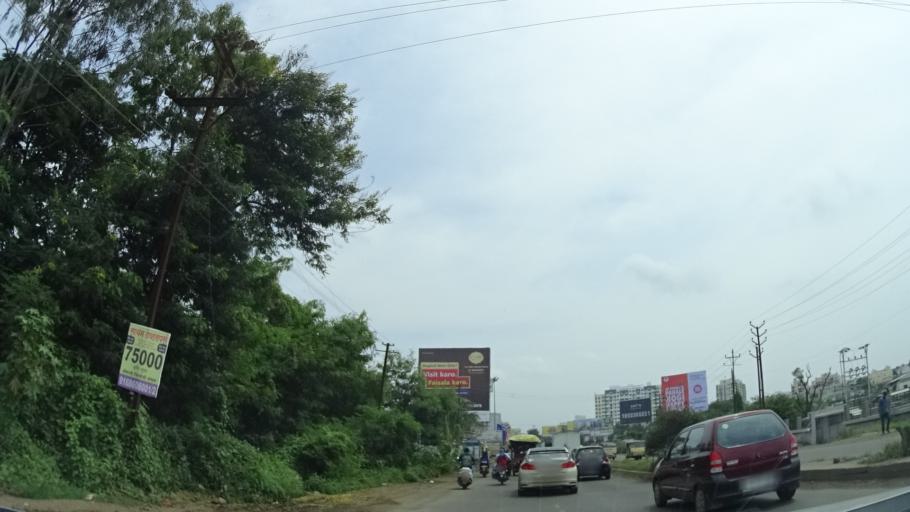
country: IN
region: Maharashtra
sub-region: Pune Division
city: Lohogaon
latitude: 18.5777
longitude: 73.9704
